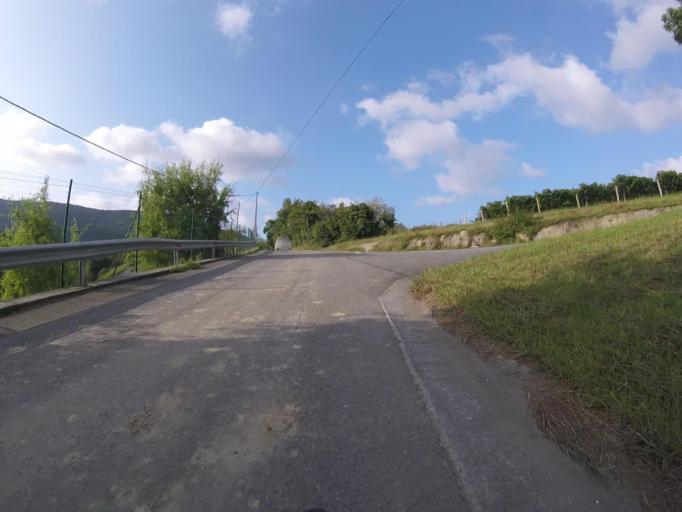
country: ES
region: Basque Country
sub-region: Provincia de Guipuzcoa
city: Fuenterrabia
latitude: 43.3480
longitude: -1.8195
